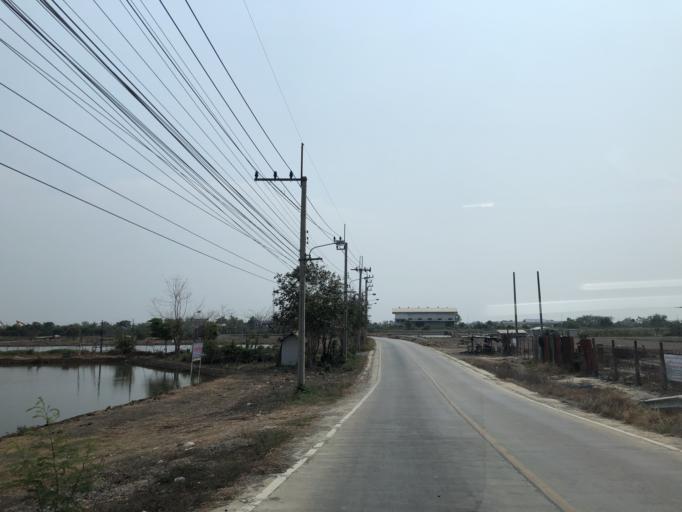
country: TH
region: Samut Prakan
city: Bang Bo
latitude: 13.5393
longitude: 100.8727
